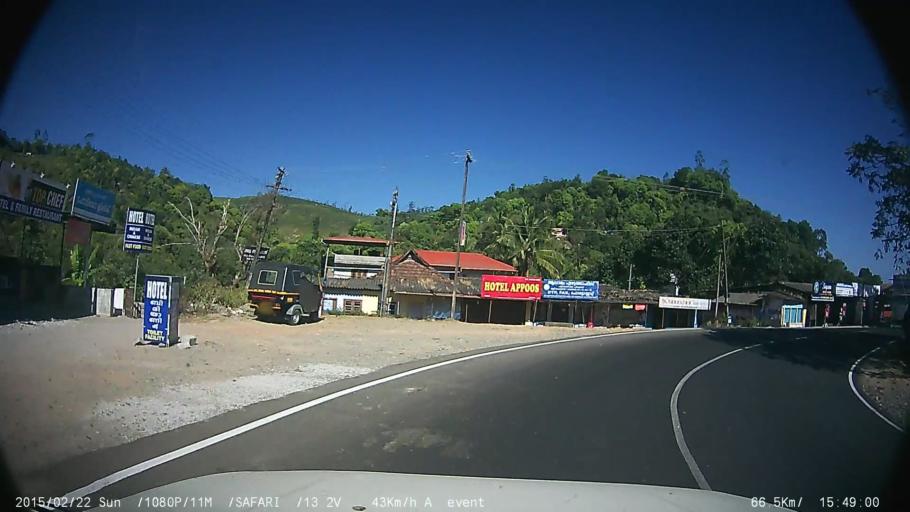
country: IN
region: Kerala
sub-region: Kottayam
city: Erattupetta
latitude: 9.5724
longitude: 76.9952
